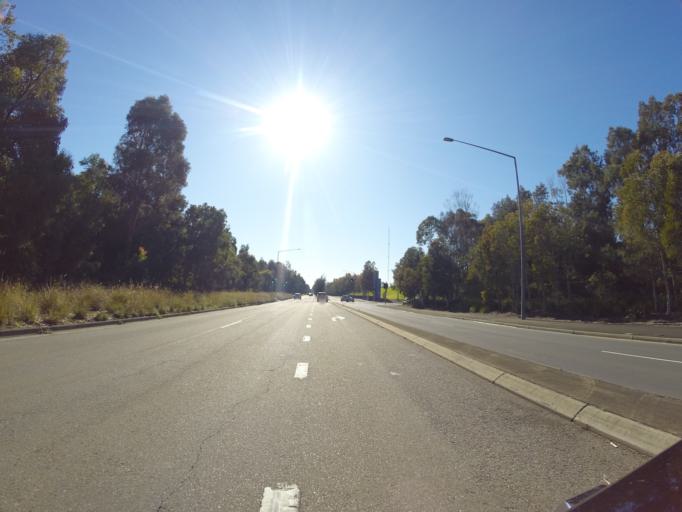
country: AU
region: New South Wales
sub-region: Auburn
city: Auburn
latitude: -33.8425
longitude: 151.0583
